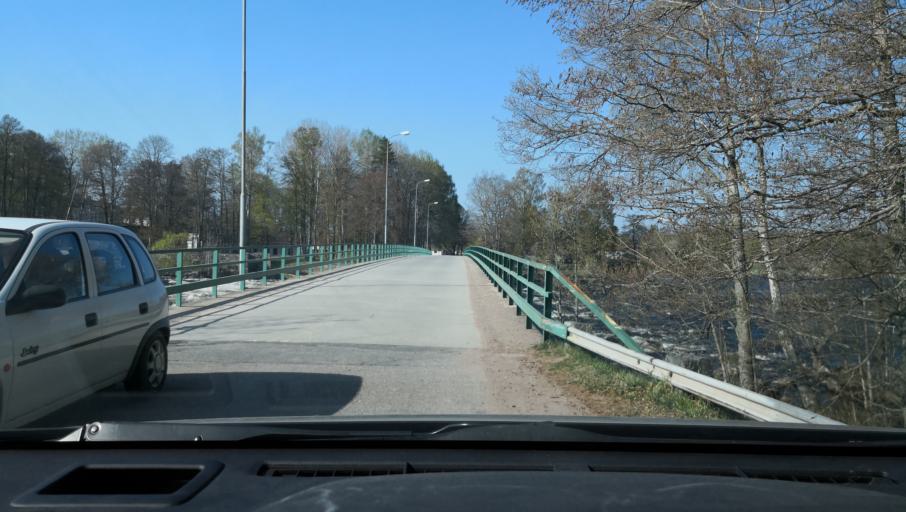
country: SE
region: Uppsala
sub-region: Heby Kommun
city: Tarnsjo
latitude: 60.2854
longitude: 16.8843
